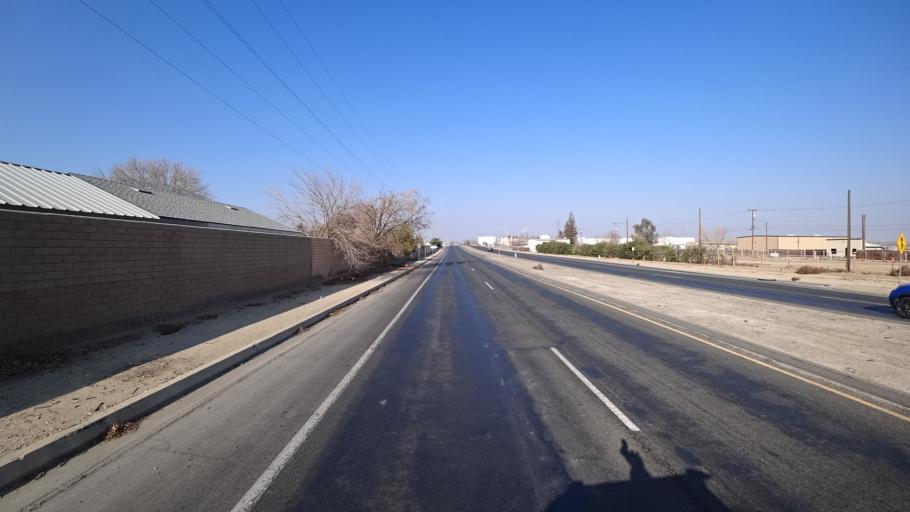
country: US
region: California
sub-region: Kern County
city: Oildale
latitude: 35.4126
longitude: -119.0129
